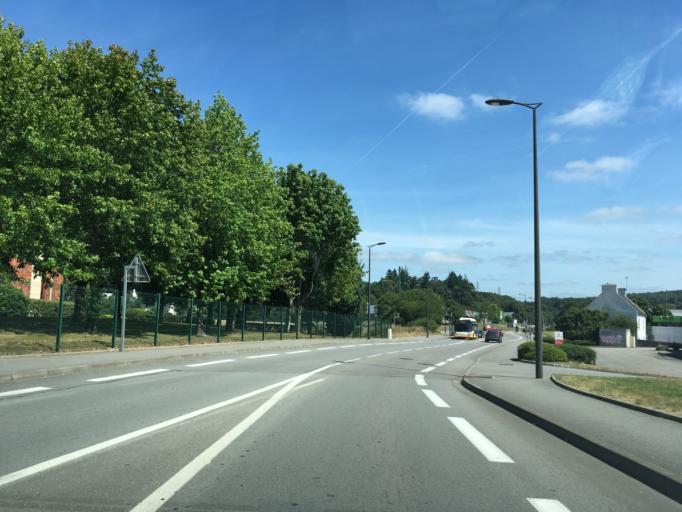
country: FR
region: Brittany
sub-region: Departement du Finistere
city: Quimper
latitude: 48.0143
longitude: -4.0877
